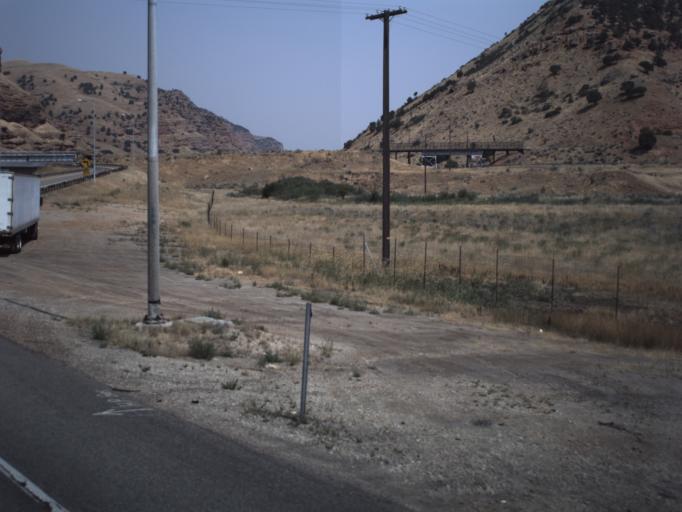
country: US
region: Utah
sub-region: Summit County
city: Coalville
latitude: 40.9690
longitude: -111.4389
